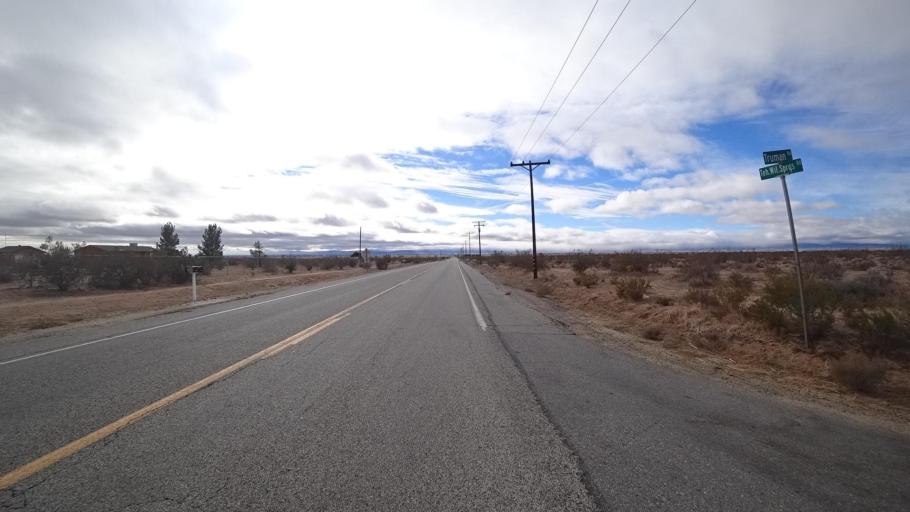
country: US
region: California
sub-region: Kern County
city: Rosamond
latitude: 34.8744
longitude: -118.2910
